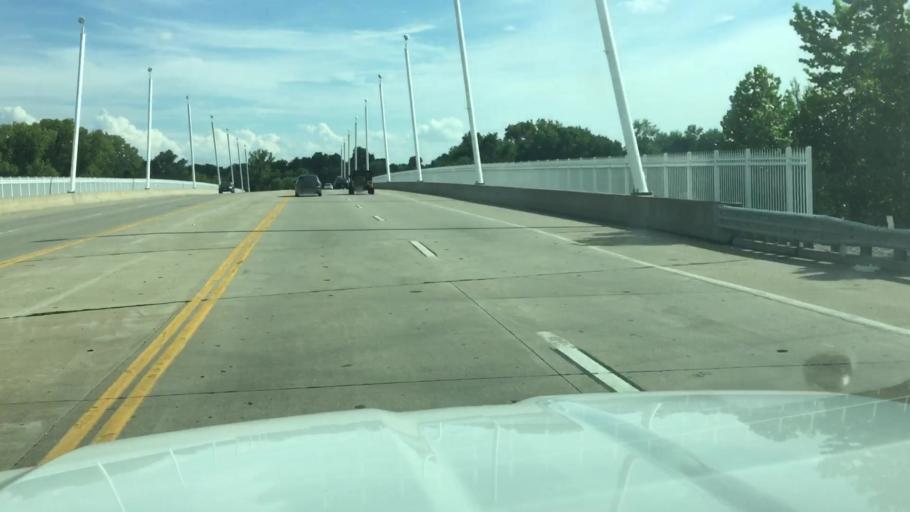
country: US
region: Missouri
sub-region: Jefferson County
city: Arnold
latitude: 38.4579
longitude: -90.3606
